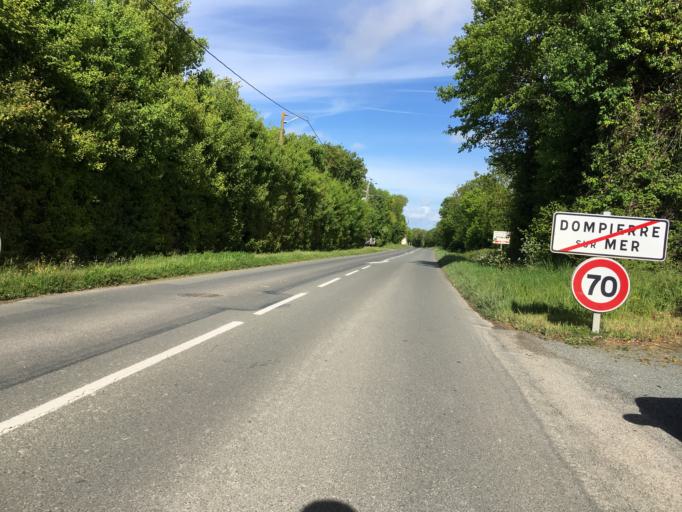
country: FR
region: Poitou-Charentes
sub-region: Departement de la Charente-Maritime
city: Dompierre-sur-Mer
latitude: 46.1768
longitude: -1.0613
